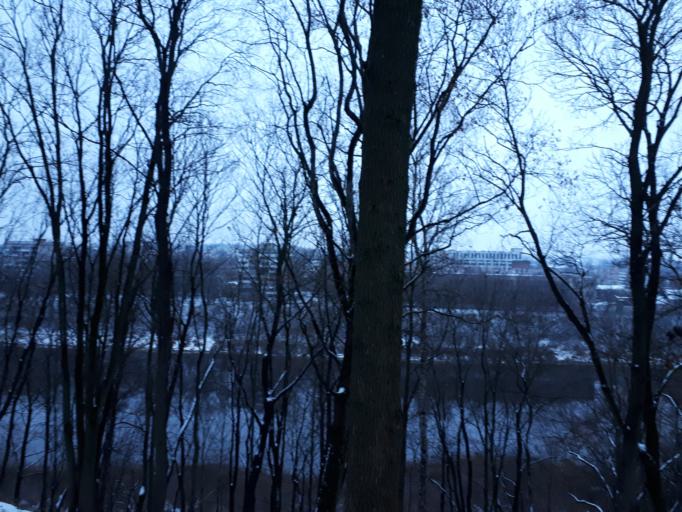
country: BY
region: Vitebsk
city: Vitebsk
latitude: 55.1995
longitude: 30.2021
